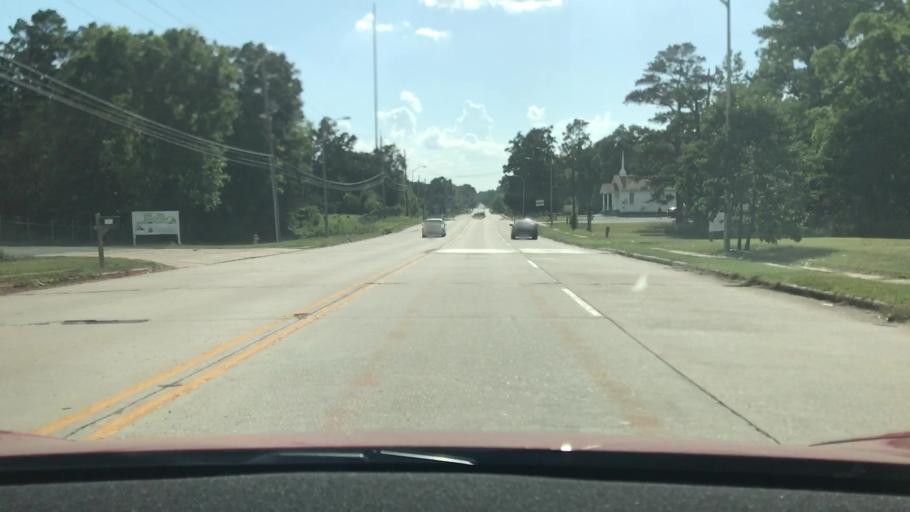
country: US
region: Louisiana
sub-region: Bossier Parish
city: Bossier City
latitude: 32.4130
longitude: -93.7698
